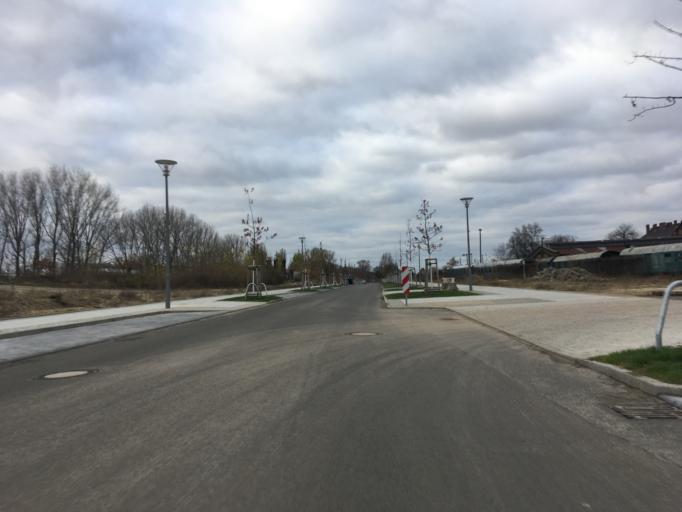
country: DE
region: Berlin
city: Niederschoneweide
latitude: 52.4461
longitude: 13.5210
